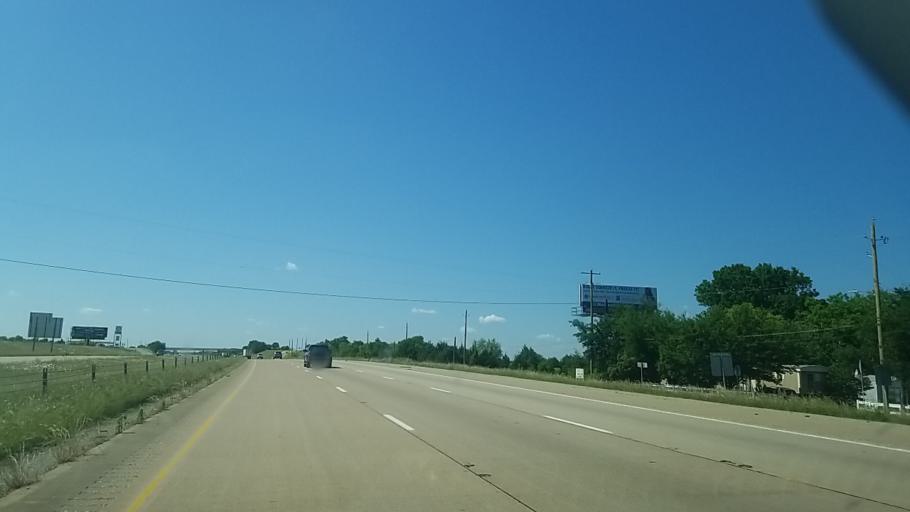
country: US
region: Texas
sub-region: Ellis County
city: Ennis
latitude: 32.3550
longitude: -96.6284
